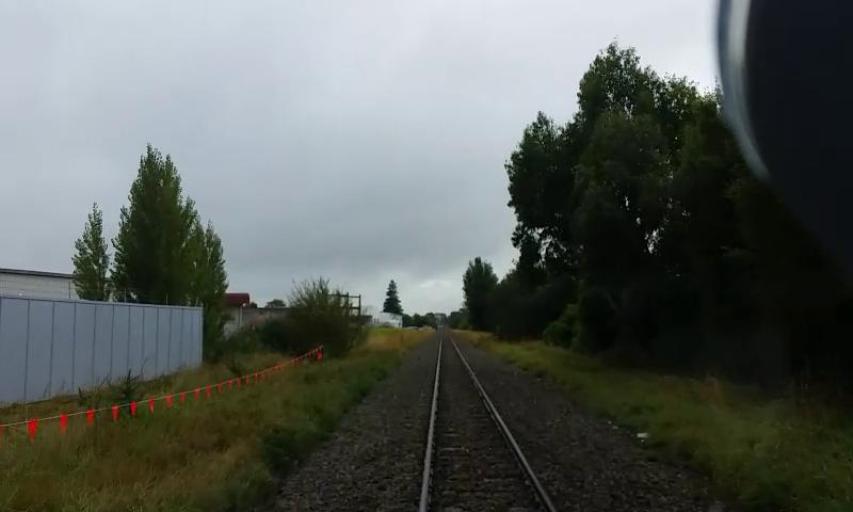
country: NZ
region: Canterbury
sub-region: Christchurch City
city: Christchurch
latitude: -43.5338
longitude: 172.6093
